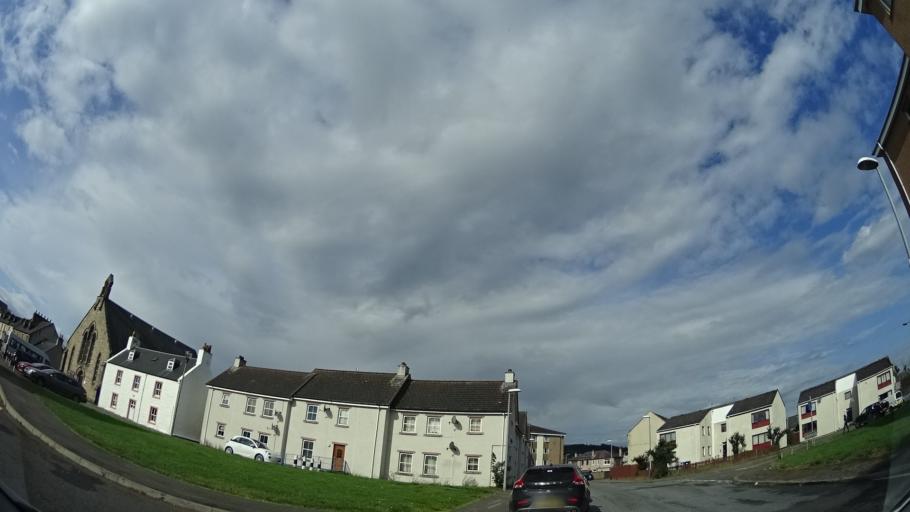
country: GB
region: Scotland
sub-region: Highland
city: Inverness
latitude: 57.4830
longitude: -4.2348
